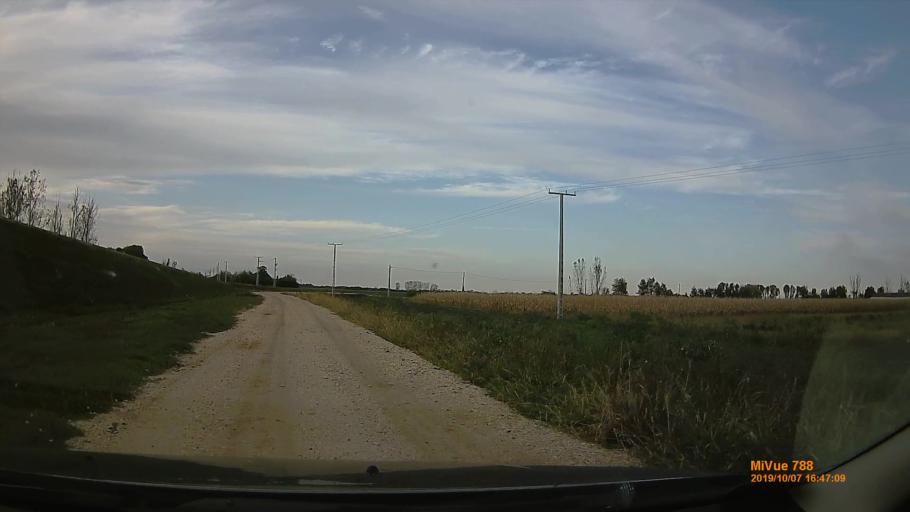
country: HU
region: Bekes
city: Szarvas
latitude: 46.8201
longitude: 20.6049
